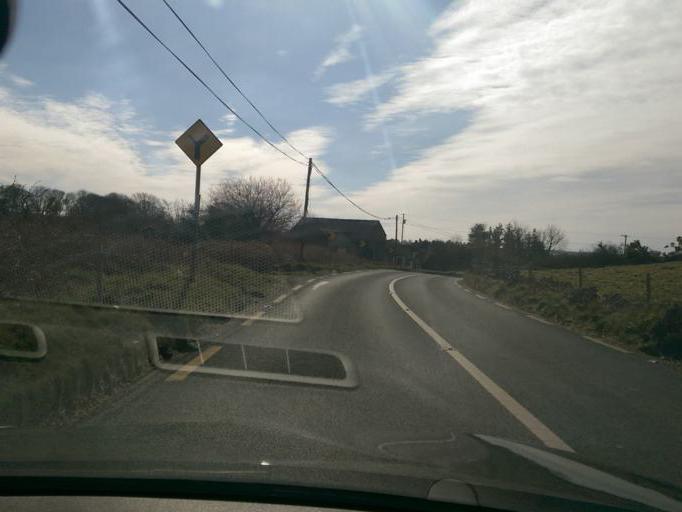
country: IE
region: Connaught
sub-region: County Galway
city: Athenry
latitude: 53.4626
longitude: -8.6708
